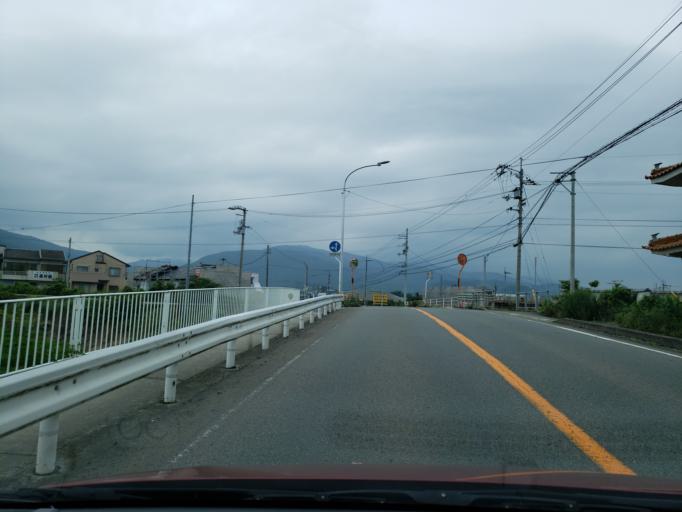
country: JP
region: Tokushima
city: Kamojimacho-jogejima
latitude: 34.1056
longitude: 134.3470
